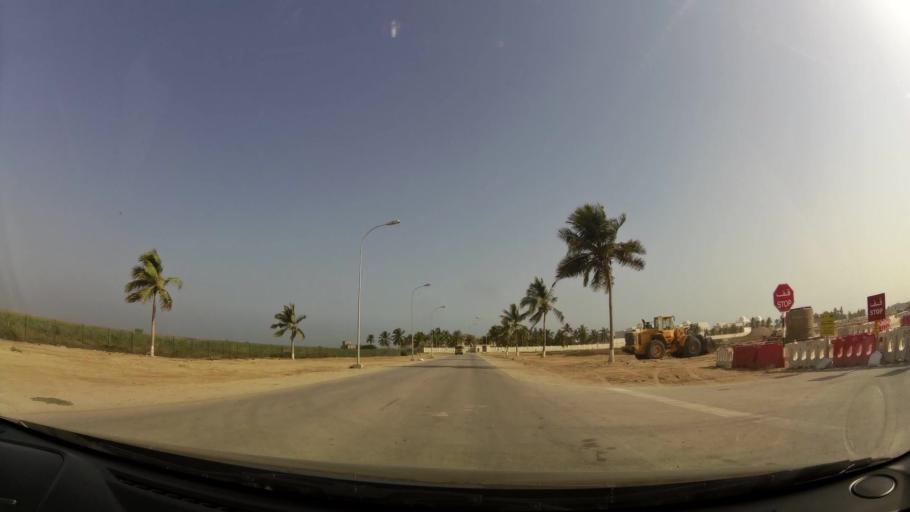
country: OM
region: Zufar
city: Salalah
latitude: 16.9984
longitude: 54.0653
